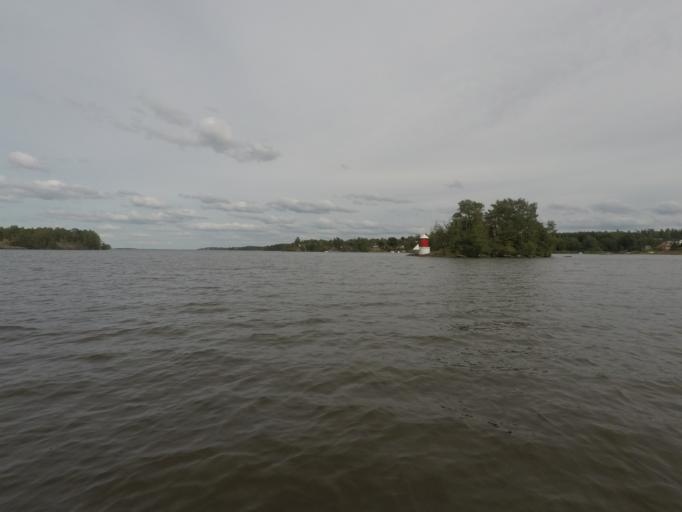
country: SE
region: Soedermanland
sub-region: Eskilstuna Kommun
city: Kvicksund
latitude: 59.4549
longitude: 16.3575
